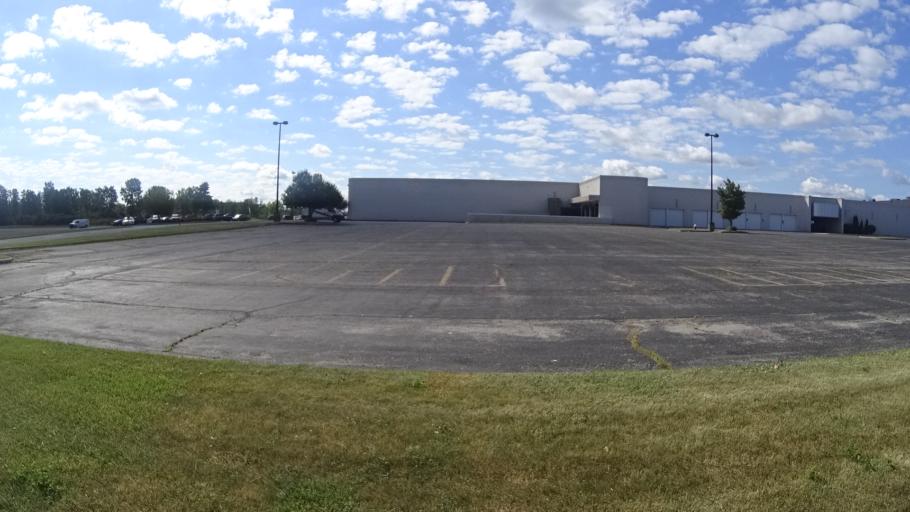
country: US
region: Ohio
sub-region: Erie County
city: Sandusky
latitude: 41.4209
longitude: -82.6709
